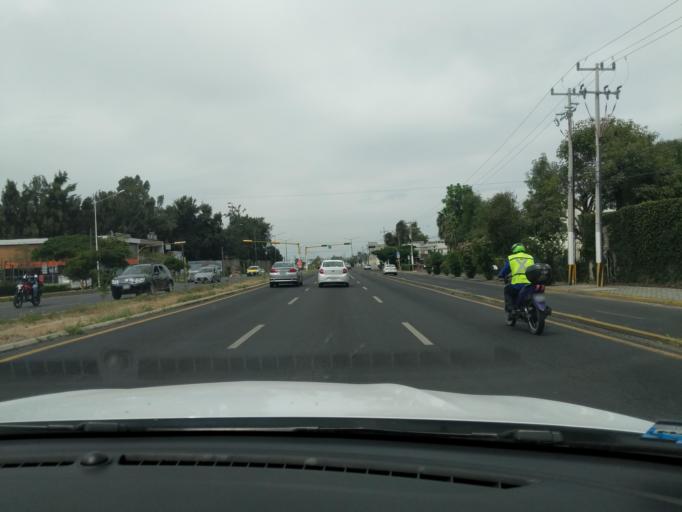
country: MX
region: Jalisco
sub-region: Zapopan
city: Puerta del Llano
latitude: 20.7861
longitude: -103.4691
